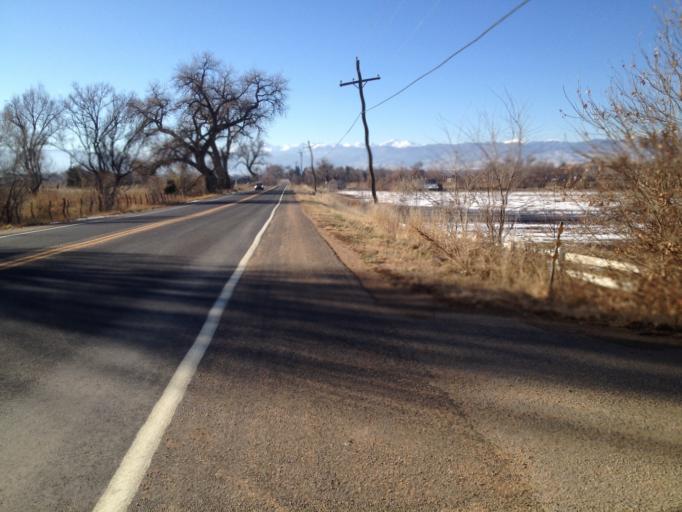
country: US
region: Colorado
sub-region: Boulder County
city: Gunbarrel
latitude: 40.0402
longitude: -105.1398
